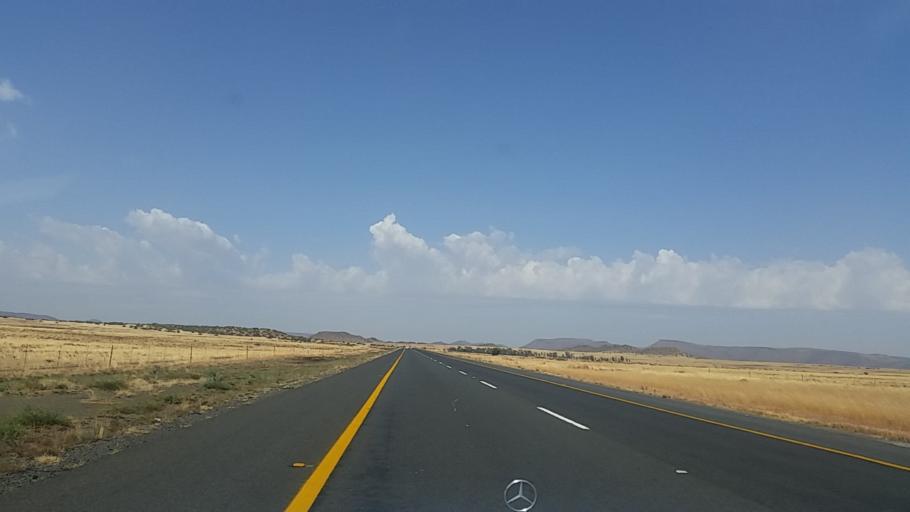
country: ZA
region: Orange Free State
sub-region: Xhariep District Municipality
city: Trompsburg
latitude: -30.4170
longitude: 25.6490
